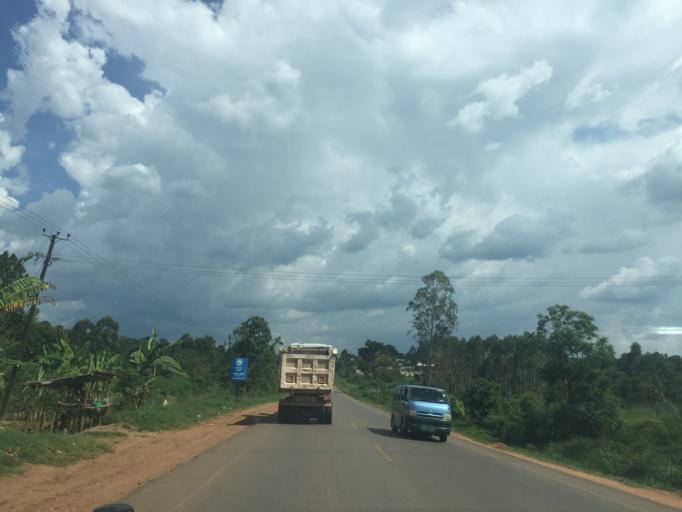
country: UG
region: Central Region
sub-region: Luwero District
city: Wobulenzi
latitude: 0.7383
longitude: 32.5194
